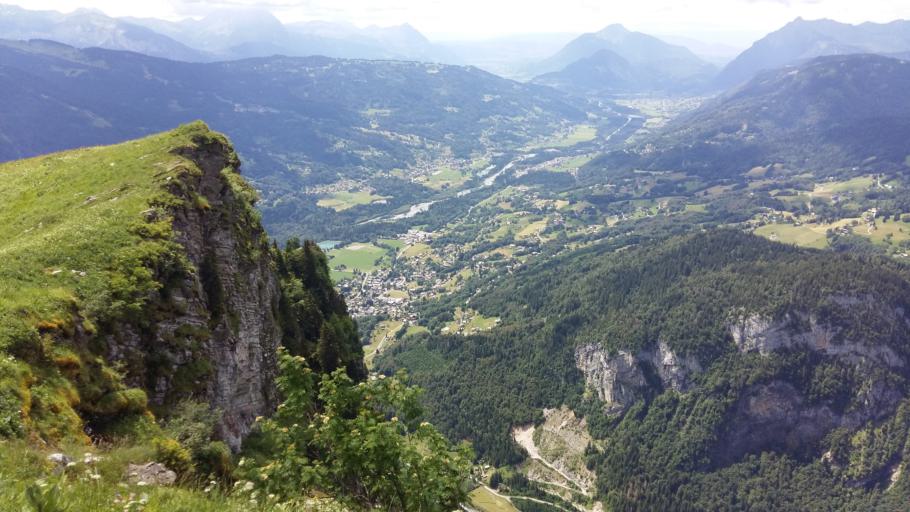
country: FR
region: Rhone-Alpes
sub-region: Departement de la Haute-Savoie
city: Samoens
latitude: 46.0917
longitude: 6.7597
